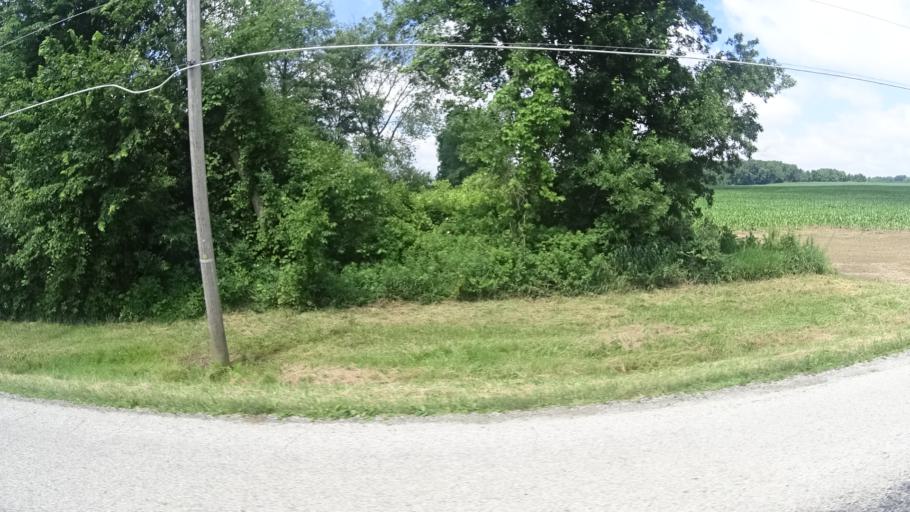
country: US
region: Ohio
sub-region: Huron County
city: Wakeman
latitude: 41.2985
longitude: -82.3630
